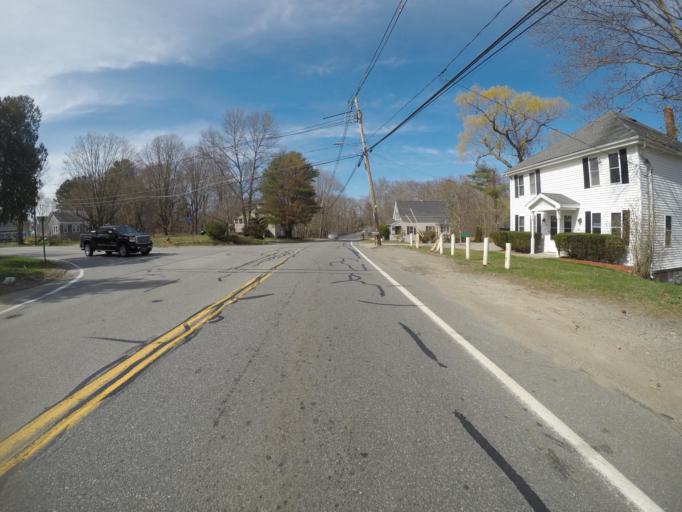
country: US
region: Massachusetts
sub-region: Bristol County
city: Easton
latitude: 42.0398
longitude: -71.0680
